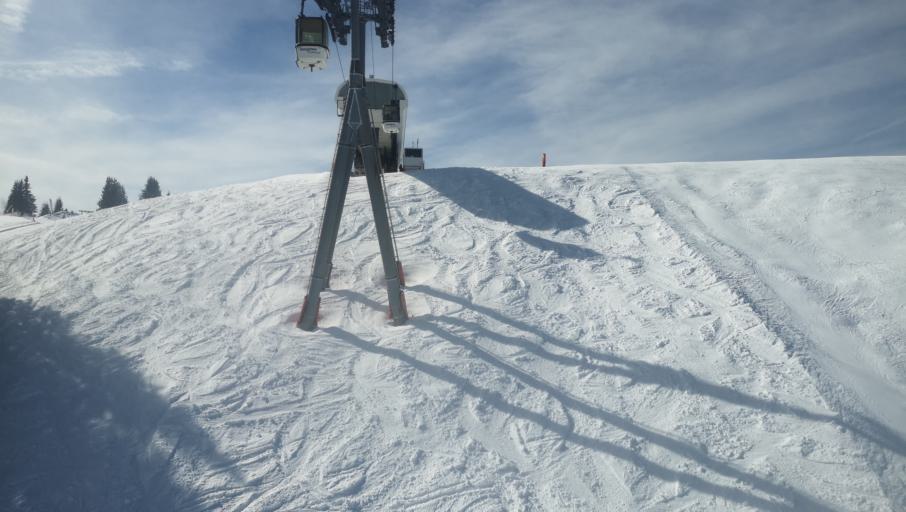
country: FR
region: Rhone-Alpes
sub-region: Departement de la Haute-Savoie
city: Megeve
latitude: 45.8332
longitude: 6.6150
